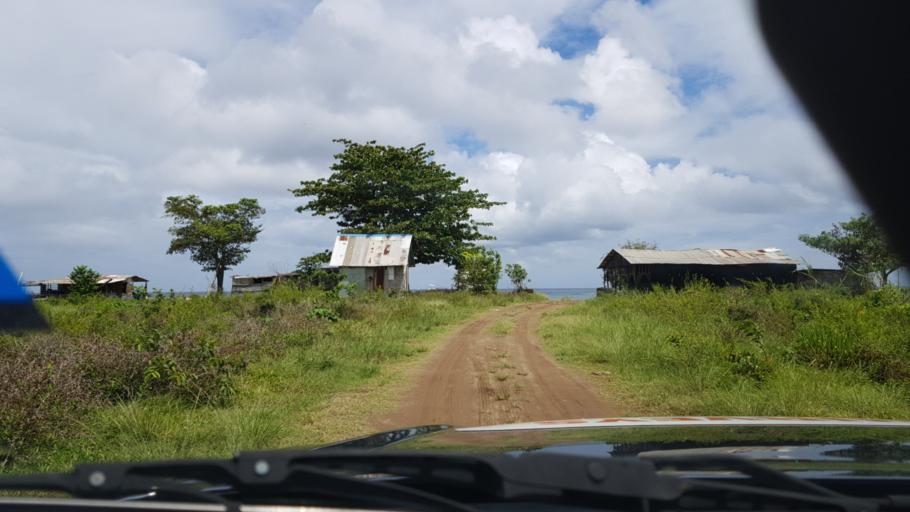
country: LC
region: Anse-la-Raye
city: Anse La Raye
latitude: 13.9578
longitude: -61.0330
